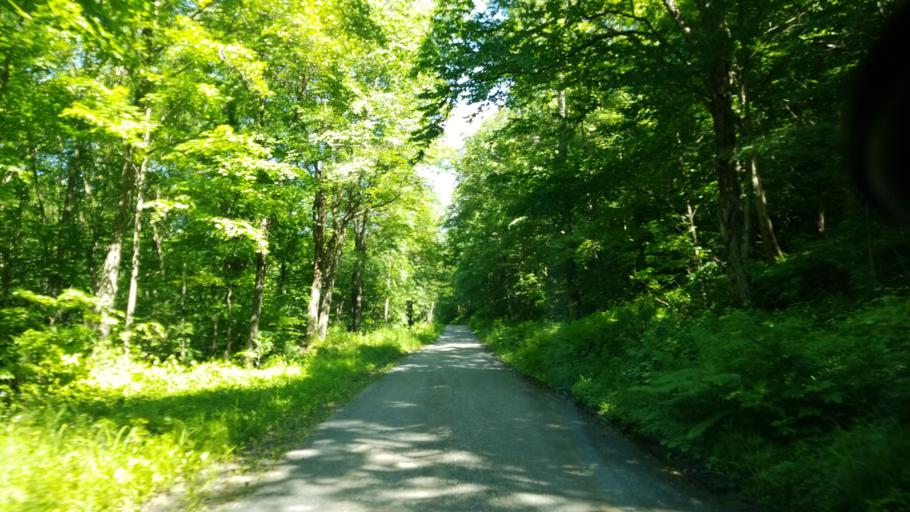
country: US
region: Pennsylvania
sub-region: Clearfield County
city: Clearfield
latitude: 41.2188
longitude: -78.3847
